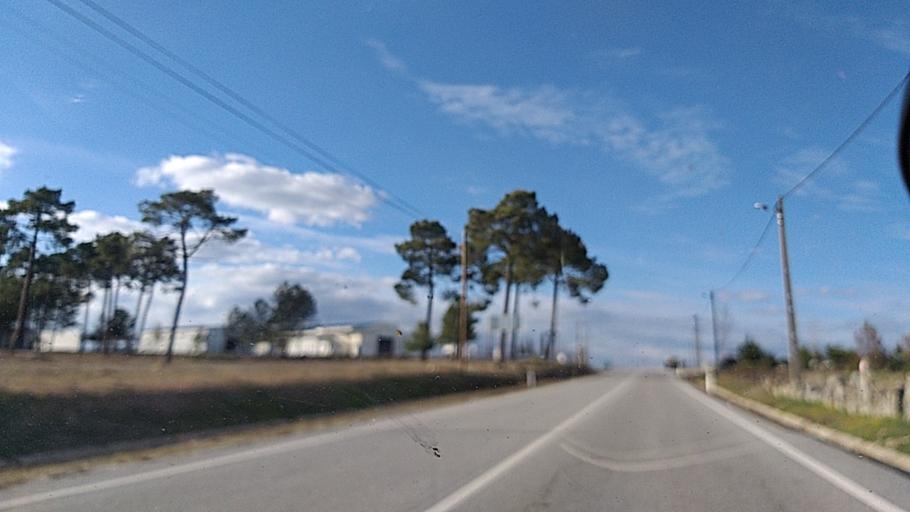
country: ES
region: Castille and Leon
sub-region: Provincia de Salamanca
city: Fuentes de Onoro
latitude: 40.6222
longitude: -6.8463
